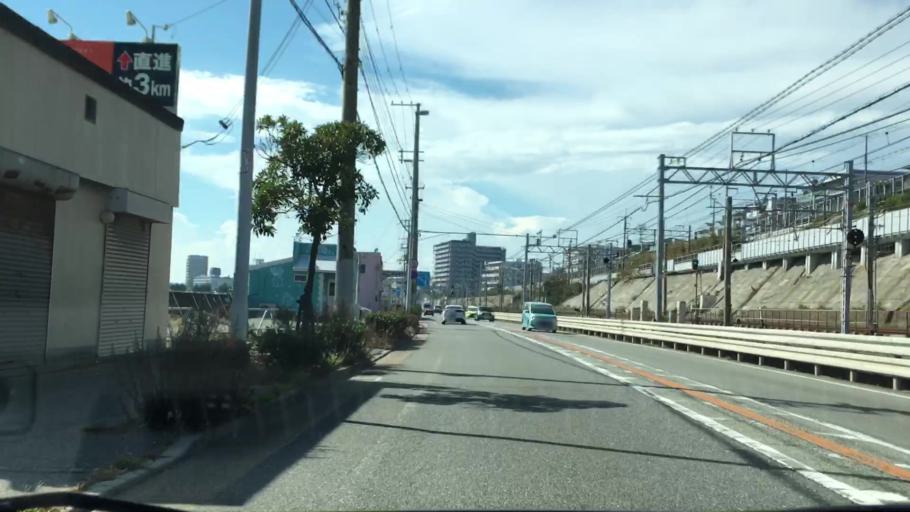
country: JP
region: Hyogo
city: Akashi
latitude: 34.6415
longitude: 135.0227
